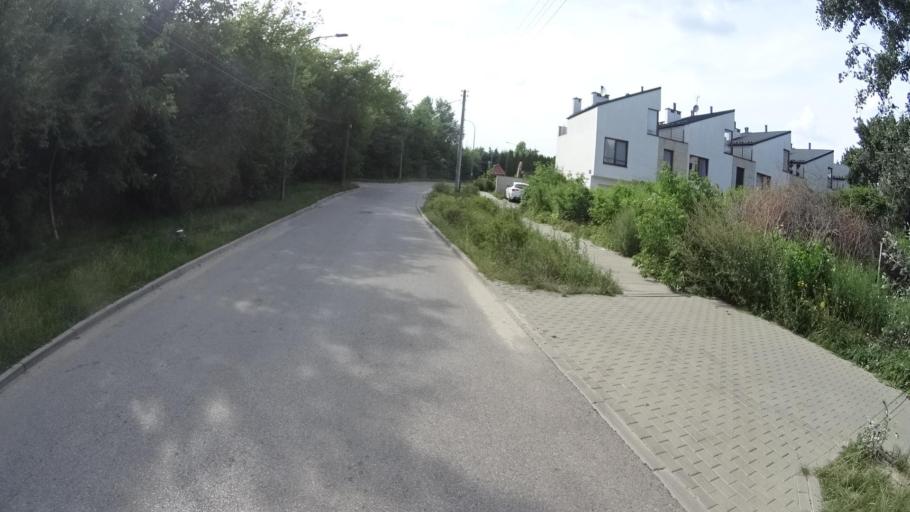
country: PL
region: Masovian Voivodeship
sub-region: Warszawa
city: Ursus
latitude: 52.2216
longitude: 20.8941
